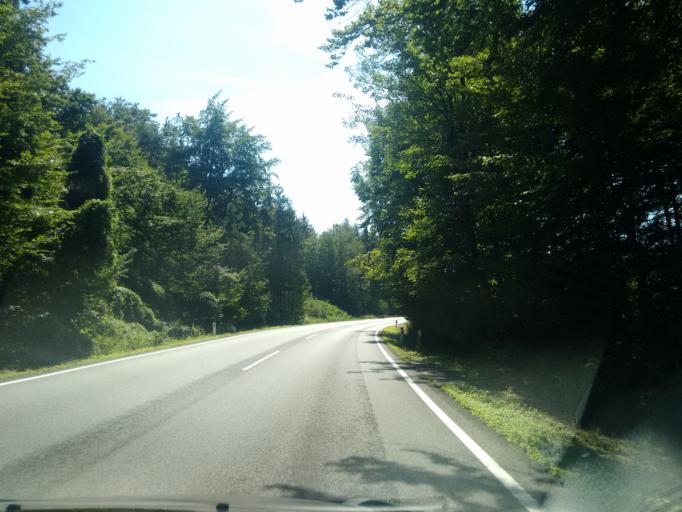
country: DE
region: Bavaria
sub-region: Upper Bavaria
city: Haiming
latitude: 48.1845
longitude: 12.8832
